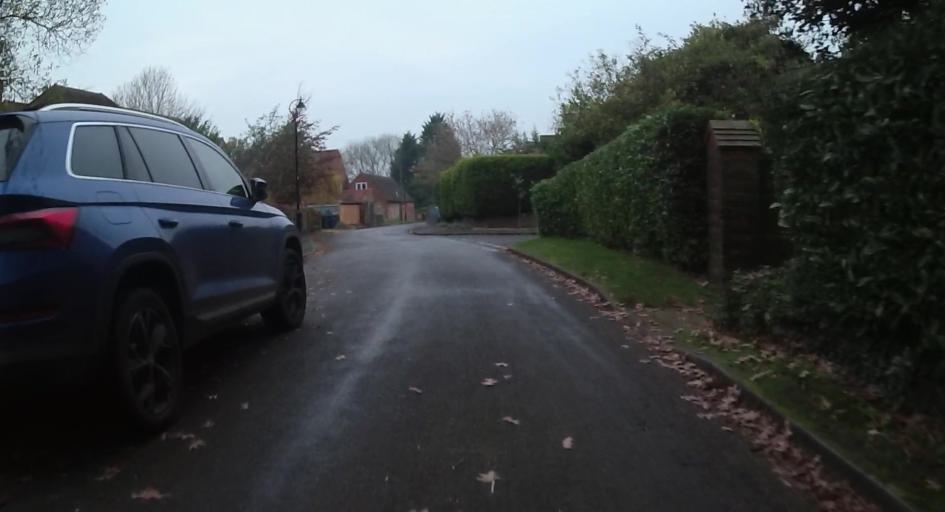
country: GB
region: England
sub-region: Surrey
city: Farnham
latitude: 51.1940
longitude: -0.8189
